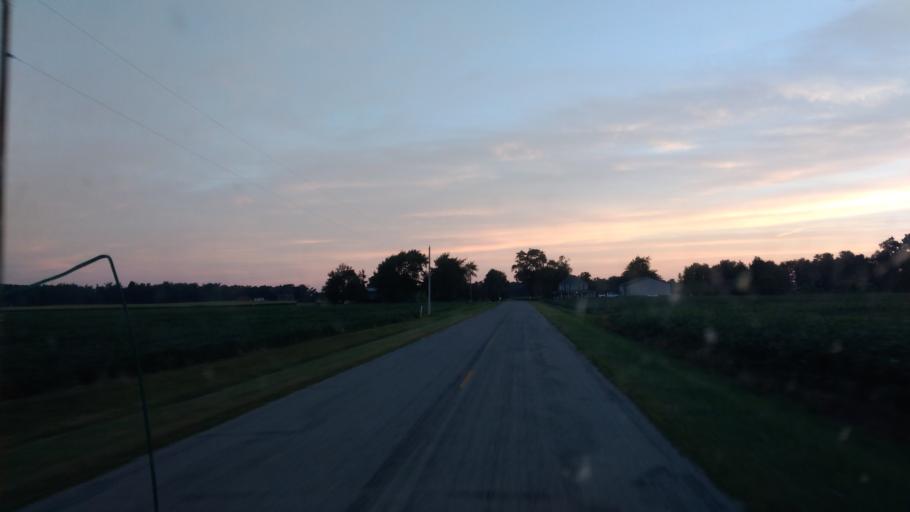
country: US
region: Indiana
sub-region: Wells County
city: Bluffton
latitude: 40.6656
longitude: -85.1263
